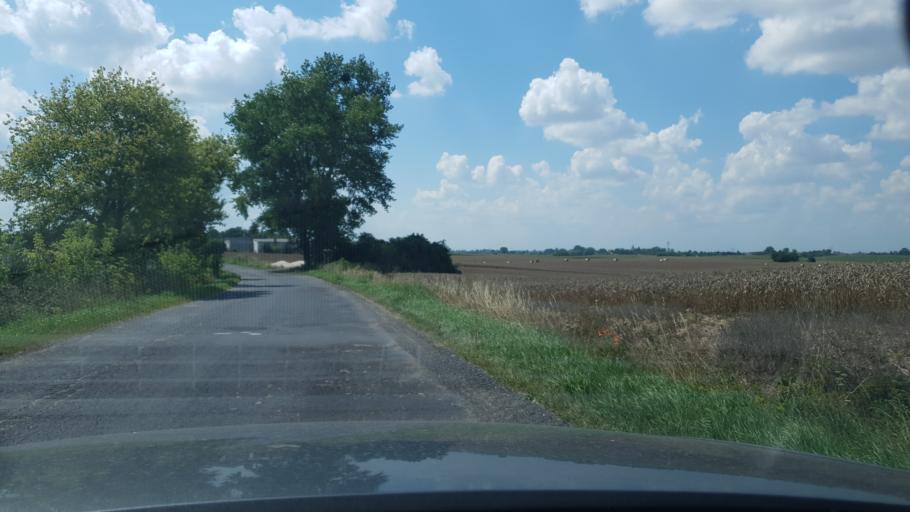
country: PL
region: Kujawsko-Pomorskie
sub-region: Powiat wabrzeski
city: Pluznica
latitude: 53.2998
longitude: 18.8055
